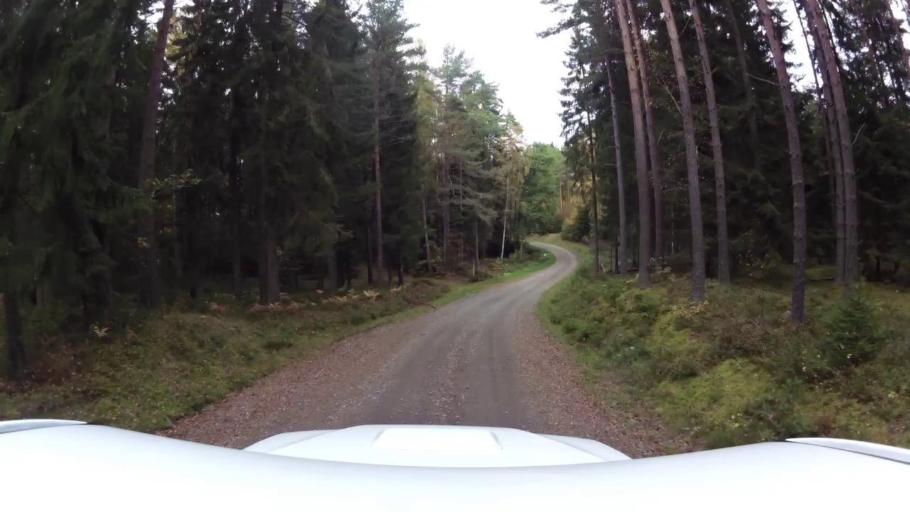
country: SE
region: OEstergoetland
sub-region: Linkopings Kommun
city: Ekangen
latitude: 58.5564
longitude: 15.6709
